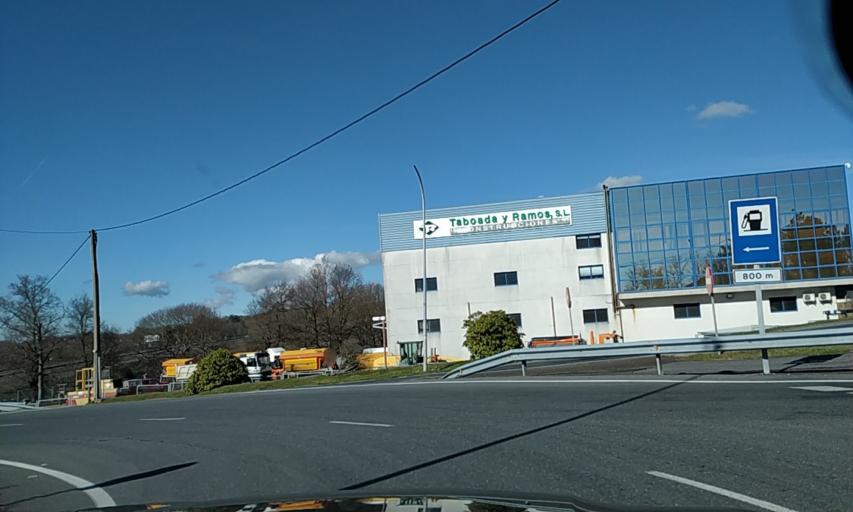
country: ES
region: Galicia
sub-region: Provincia de Pontevedra
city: Lalin
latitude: 42.6736
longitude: -8.1590
